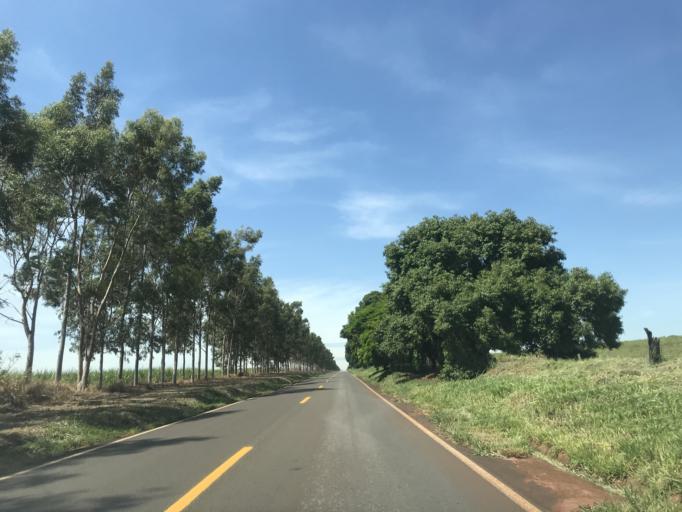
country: BR
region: Parana
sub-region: Paranavai
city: Nova Aurora
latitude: -22.8254
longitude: -52.6555
